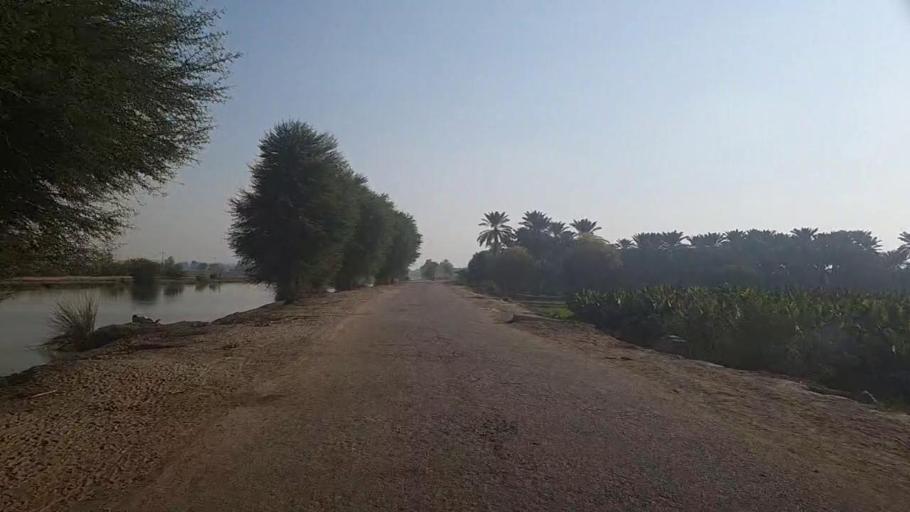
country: PK
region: Sindh
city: Kot Diji
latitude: 27.2622
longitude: 68.6754
